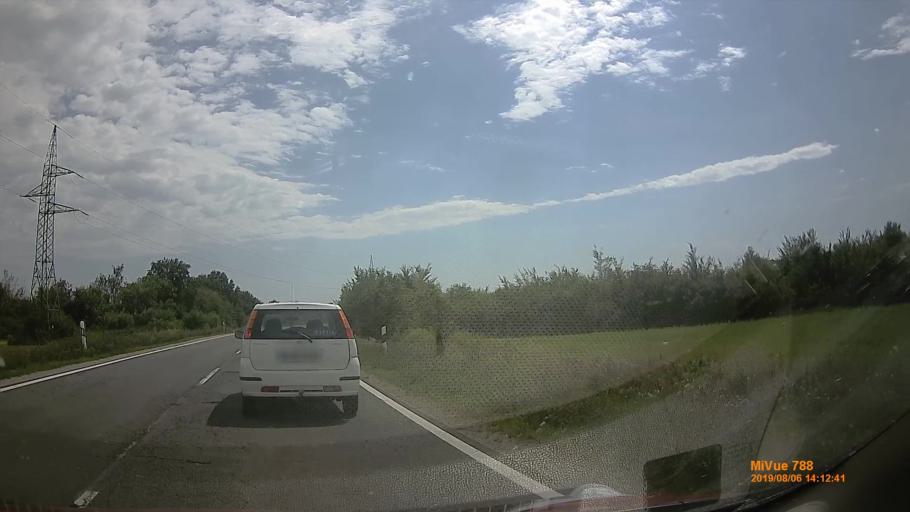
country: HU
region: Vas
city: Taplanszentkereszt
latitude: 47.2083
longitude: 16.6793
